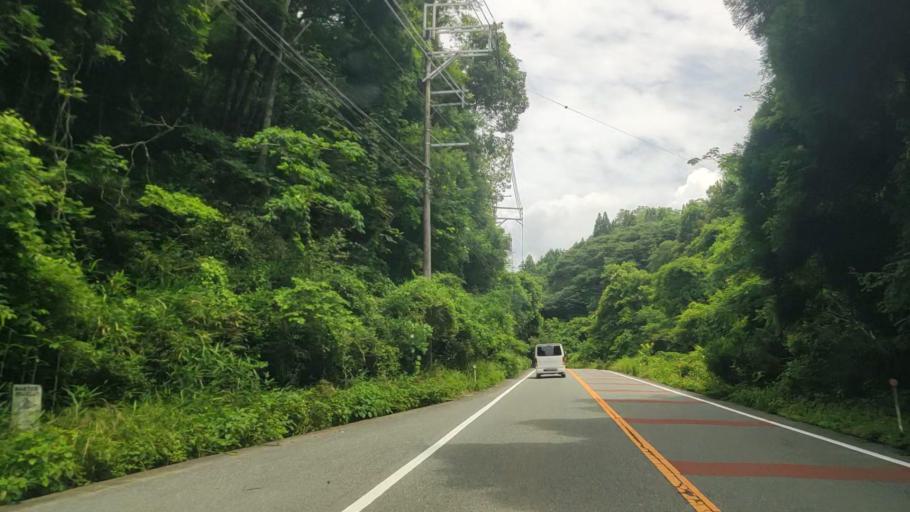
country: JP
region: Hyogo
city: Yamazakicho-nakabirose
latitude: 34.9903
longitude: 134.4080
